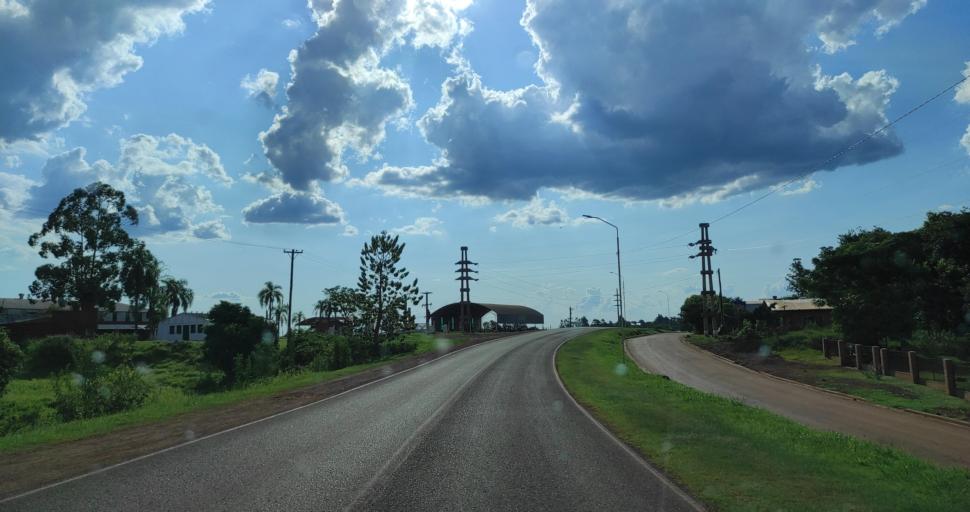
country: AR
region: Misiones
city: San Vicente
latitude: -26.3481
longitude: -54.1475
